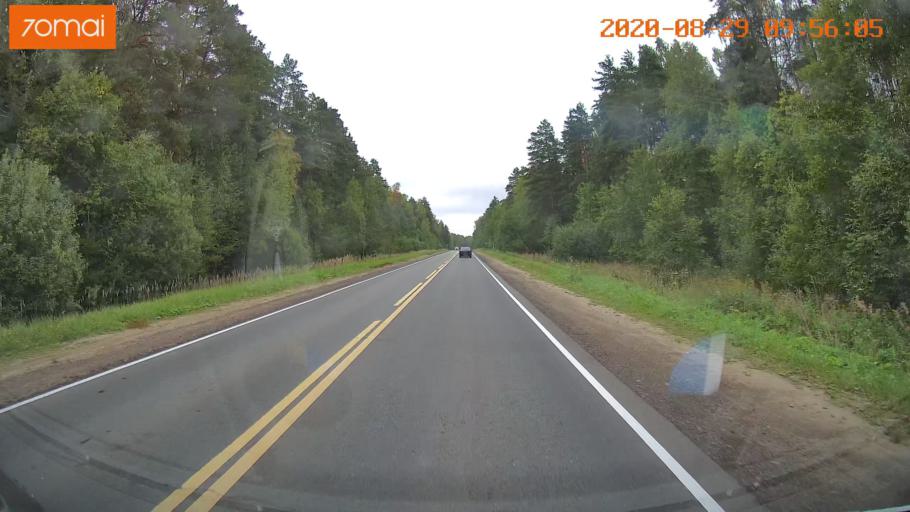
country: RU
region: Ivanovo
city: Zarechnyy
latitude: 57.4213
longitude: 42.2800
